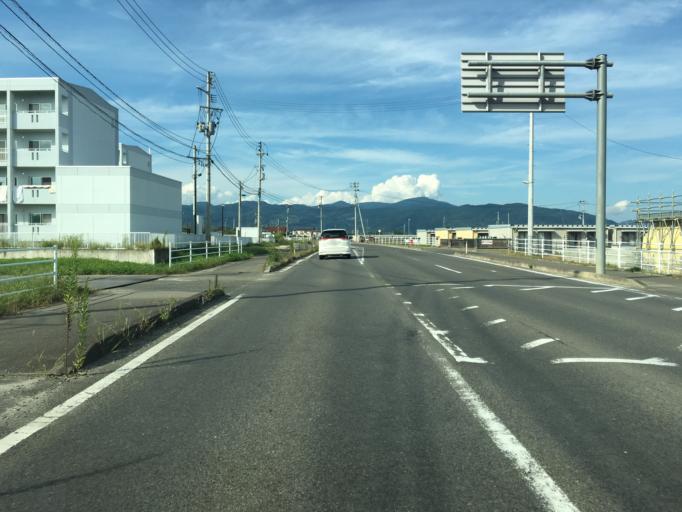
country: JP
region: Fukushima
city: Fukushima-shi
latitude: 37.7978
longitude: 140.4602
